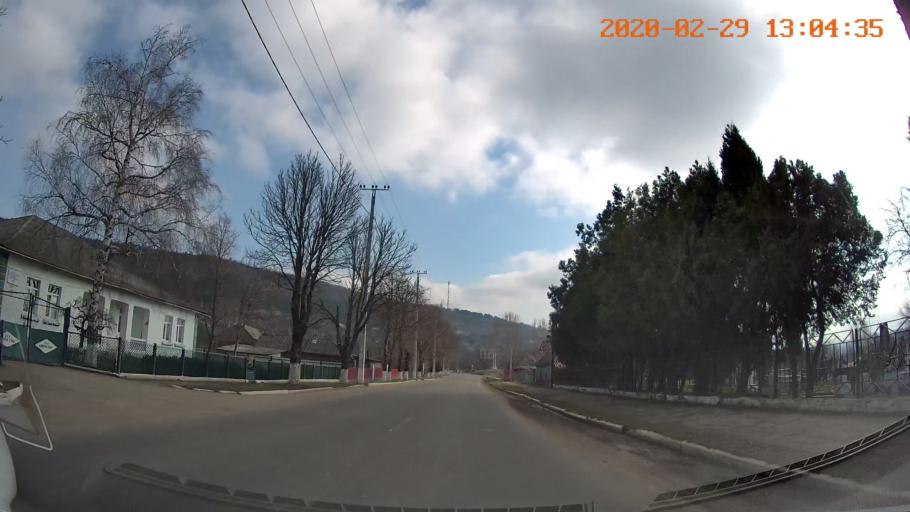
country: MD
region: Telenesti
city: Camenca
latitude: 48.0258
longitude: 28.7052
